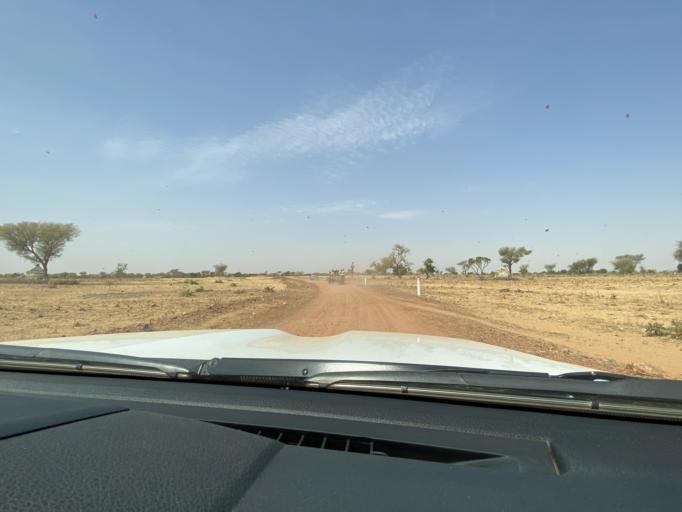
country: NE
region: Dosso
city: Birnin Gaoure
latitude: 13.2435
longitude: 2.8648
